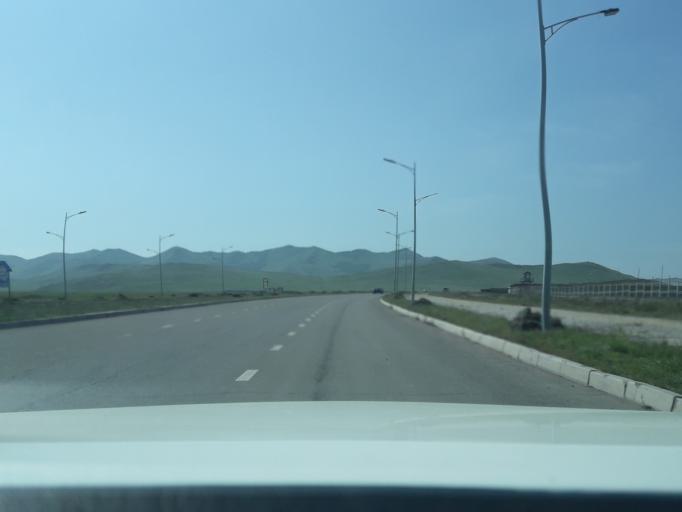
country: MN
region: Ulaanbaatar
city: Ulaanbaatar
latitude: 47.8318
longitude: 106.7866
